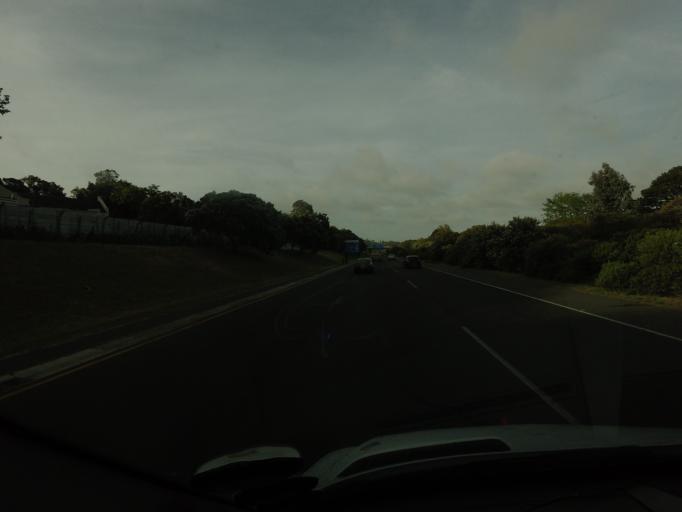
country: ZA
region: Western Cape
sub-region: City of Cape Town
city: Bergvliet
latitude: -34.0236
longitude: 18.4494
